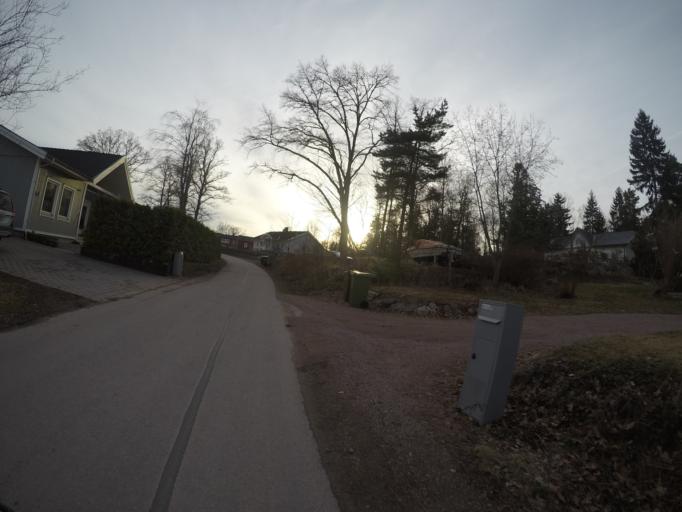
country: SE
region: Soedermanland
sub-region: Eskilstuna Kommun
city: Kvicksund
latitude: 59.4641
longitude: 16.3309
